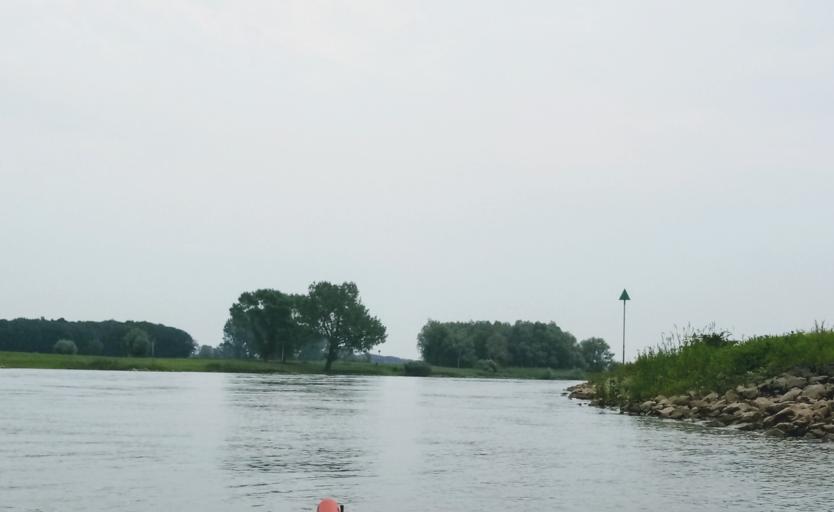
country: NL
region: Gelderland
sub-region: Gemeente Voorst
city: Voorst
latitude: 52.1890
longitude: 6.1684
